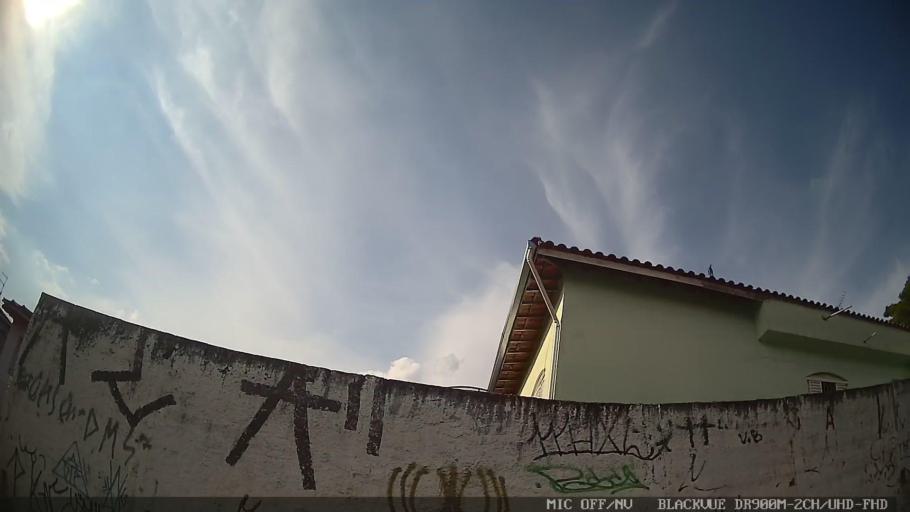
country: BR
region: Sao Paulo
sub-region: Braganca Paulista
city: Braganca Paulista
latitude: -22.9358
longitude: -46.5304
